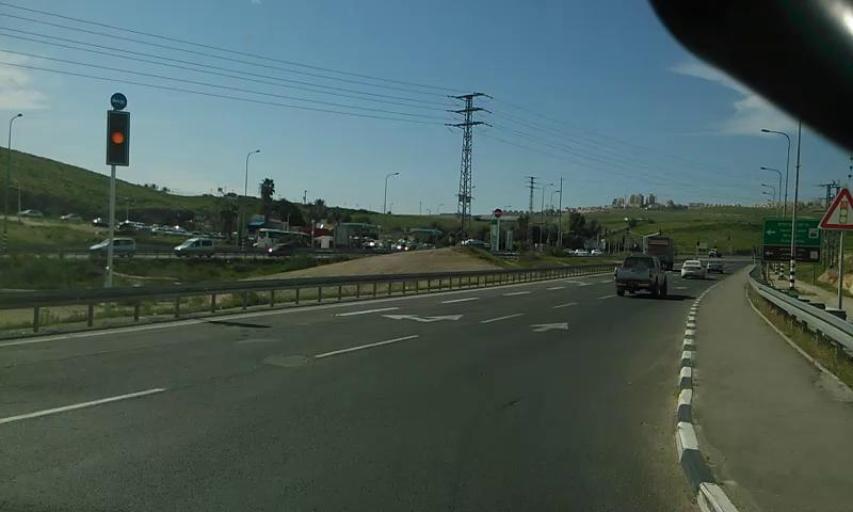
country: PS
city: Az Za`ayyim
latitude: 31.8057
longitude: 35.3259
